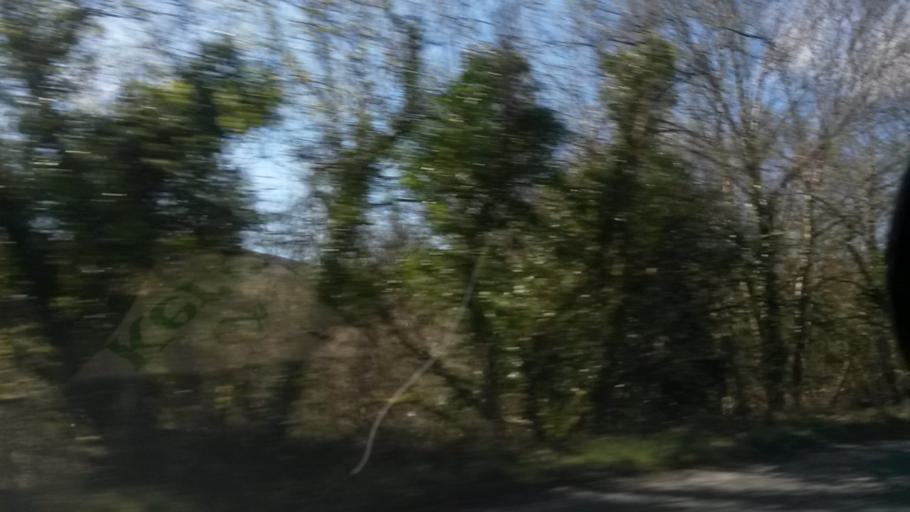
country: IE
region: Munster
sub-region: Ciarrai
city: Cill Airne
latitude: 51.9134
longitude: -9.3989
